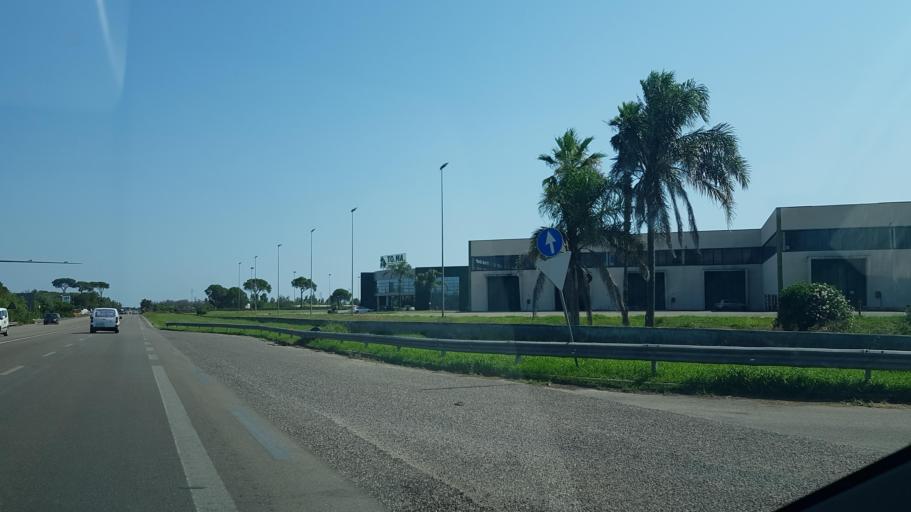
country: IT
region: Apulia
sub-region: Provincia di Lecce
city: Scorrano
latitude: 40.0987
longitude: 18.3144
